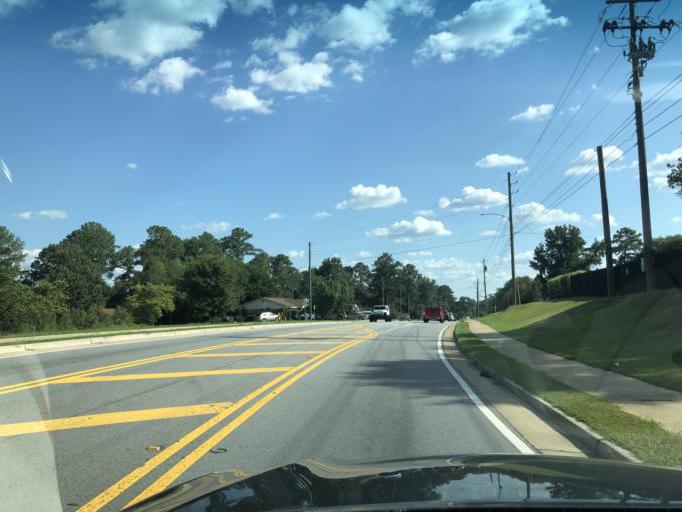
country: US
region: Georgia
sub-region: Muscogee County
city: Columbus
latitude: 32.5391
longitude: -84.9240
